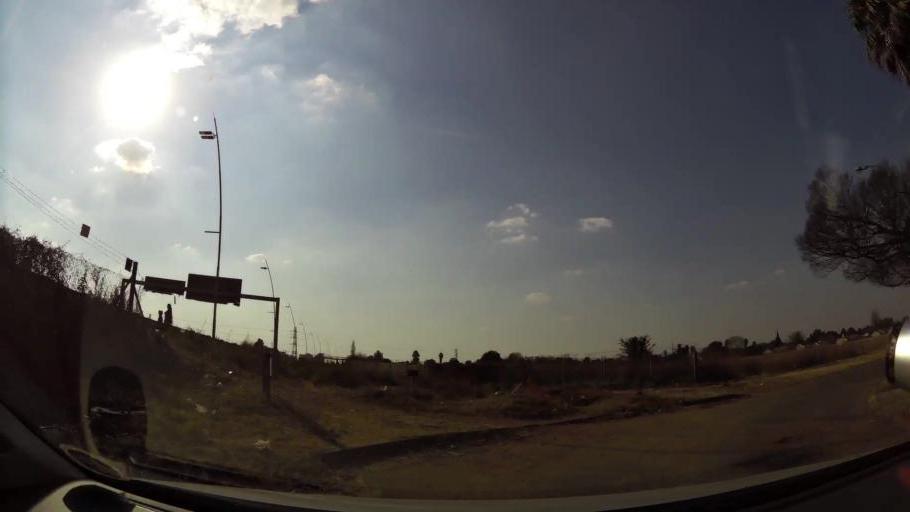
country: ZA
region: Gauteng
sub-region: City of Johannesburg Metropolitan Municipality
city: Modderfontein
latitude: -26.0841
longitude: 28.1902
